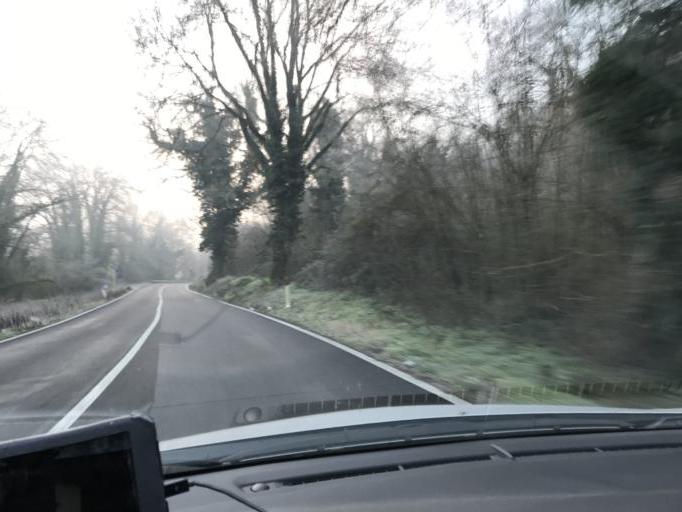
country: IT
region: Latium
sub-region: Provincia di Rieti
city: Colli sul Velino
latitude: 42.5235
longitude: 12.7340
